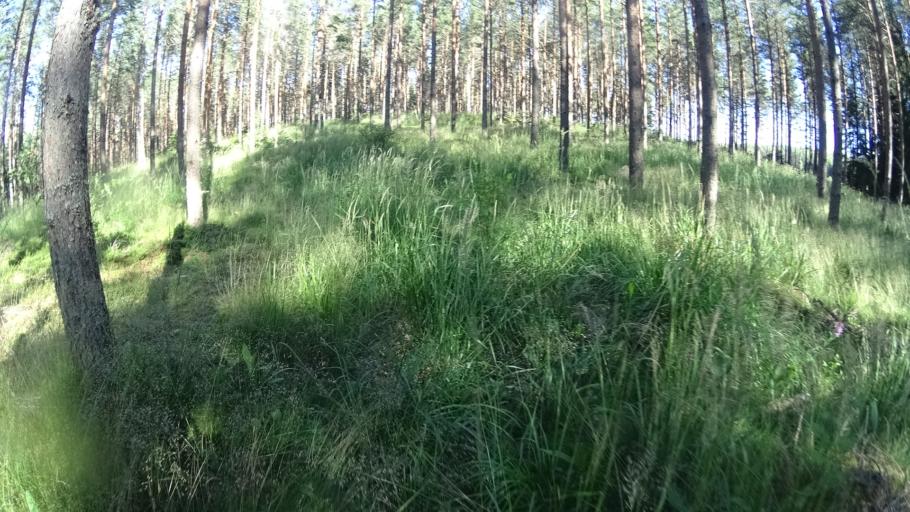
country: FI
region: Uusimaa
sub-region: Helsinki
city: Karkkila
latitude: 60.6514
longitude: 24.1542
